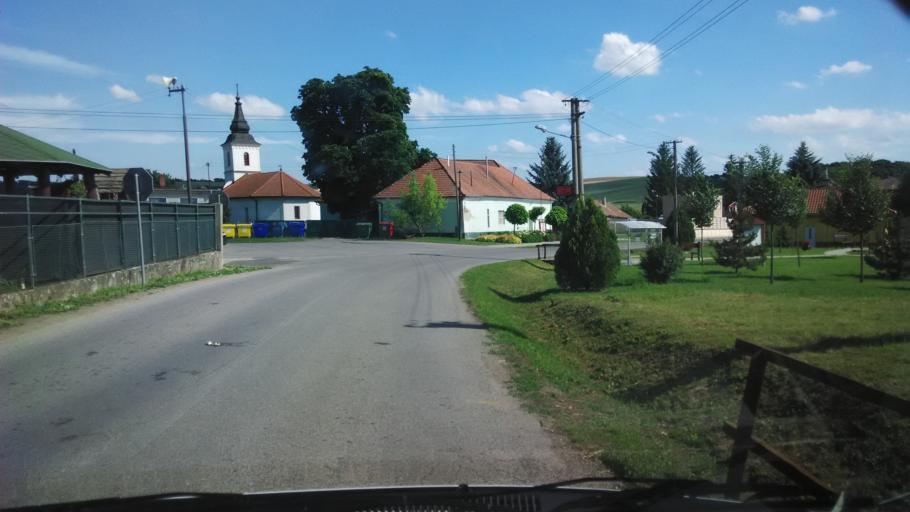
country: SK
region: Nitriansky
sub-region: Okres Nitra
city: Vrable
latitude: 48.1153
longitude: 18.3875
